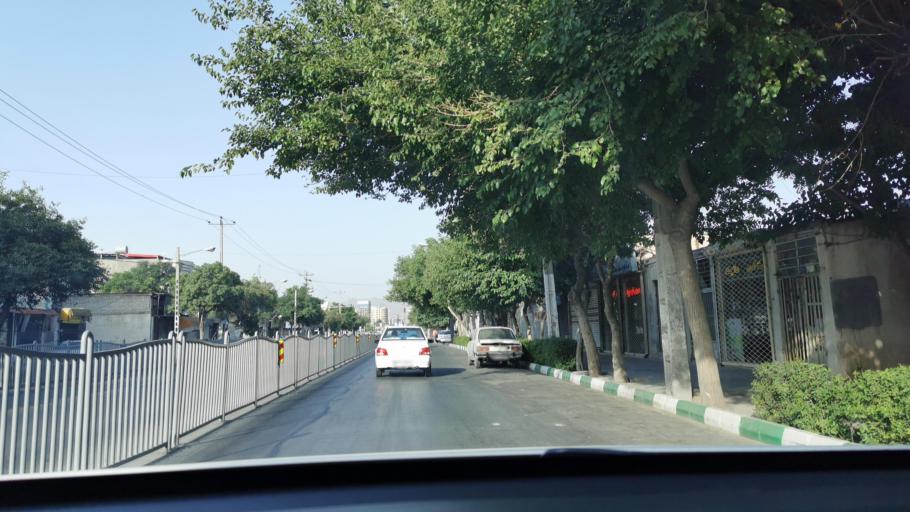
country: IR
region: Razavi Khorasan
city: Mashhad
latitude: 36.3009
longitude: 59.6361
